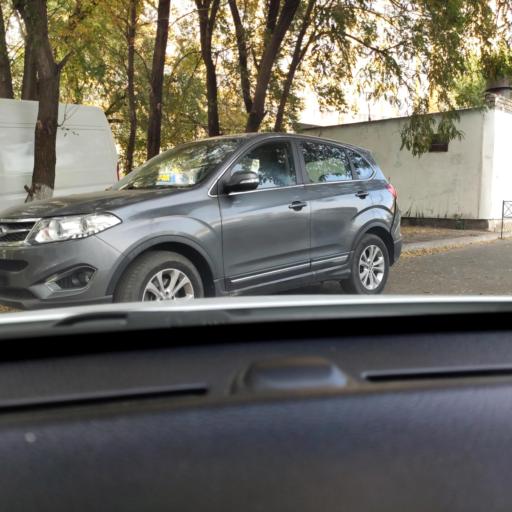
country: RU
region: Voronezj
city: Voronezh
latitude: 51.6553
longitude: 39.2388
